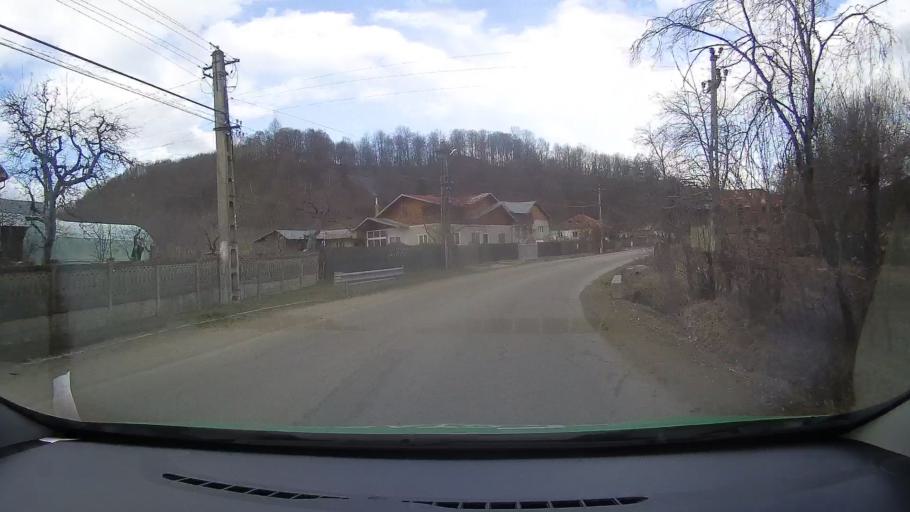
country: RO
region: Dambovita
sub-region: Comuna Visinesti
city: Visinesti
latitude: 45.0674
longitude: 25.5471
